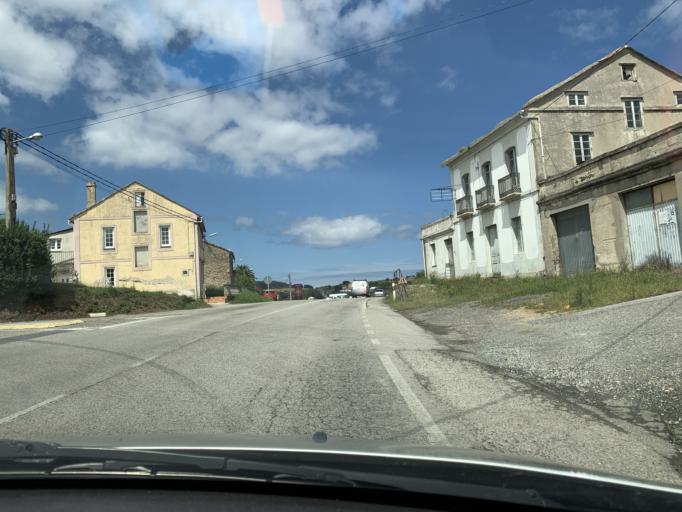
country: ES
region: Galicia
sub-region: Provincia de Lugo
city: Foz
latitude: 43.5575
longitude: -7.2707
